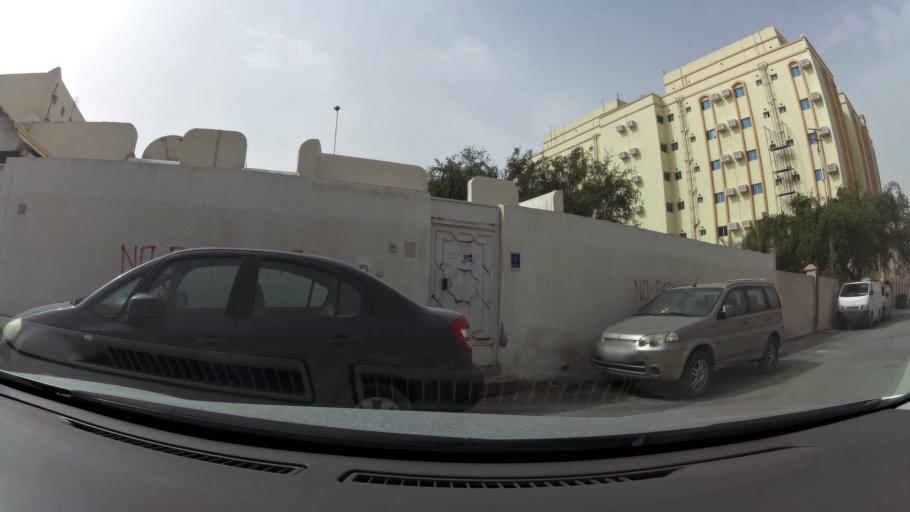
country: QA
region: Baladiyat ad Dawhah
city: Doha
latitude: 25.2723
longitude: 51.5367
